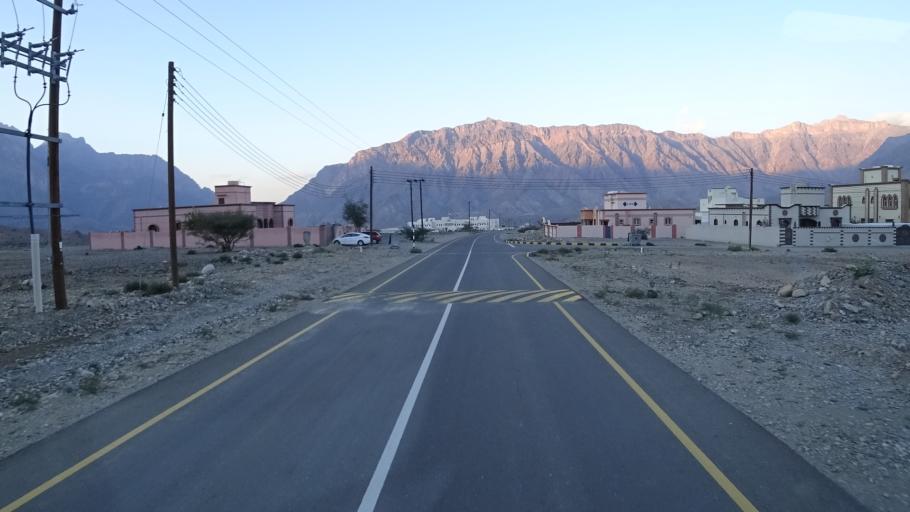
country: OM
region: Al Batinah
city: Rustaq
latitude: 23.2754
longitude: 57.3264
